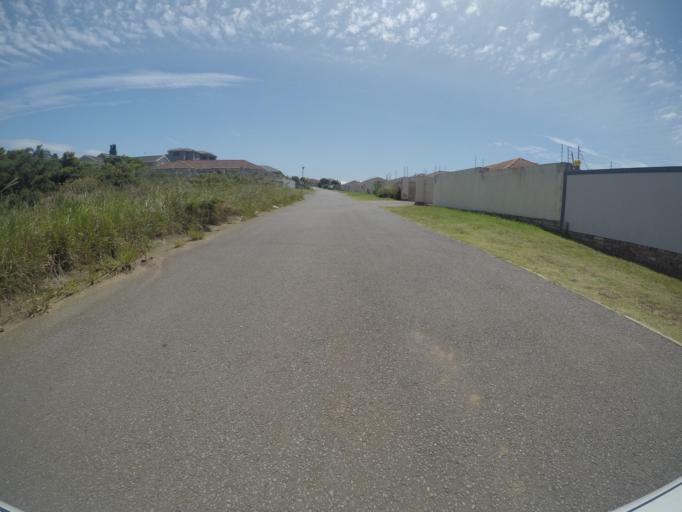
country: ZA
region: Eastern Cape
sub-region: Buffalo City Metropolitan Municipality
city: East London
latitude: -32.9432
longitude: 27.9966
